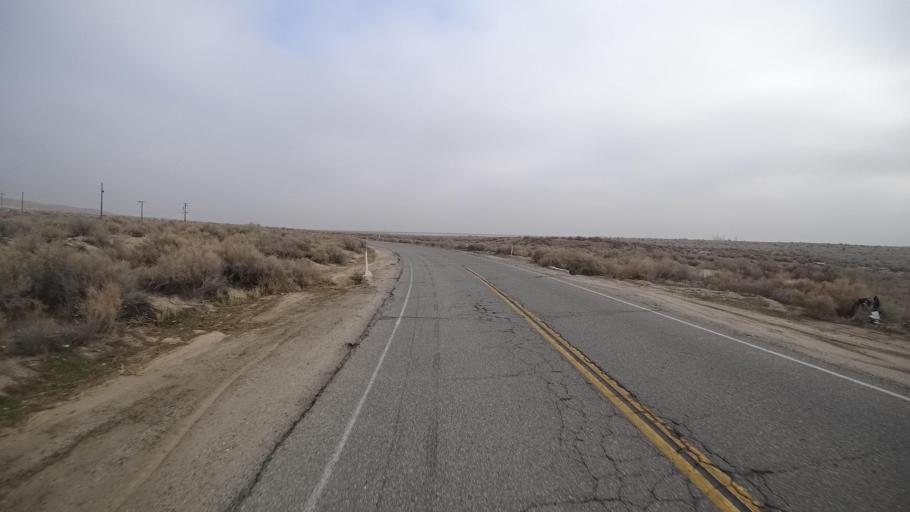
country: US
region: California
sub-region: Kern County
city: South Taft
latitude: 35.1330
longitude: -119.4049
